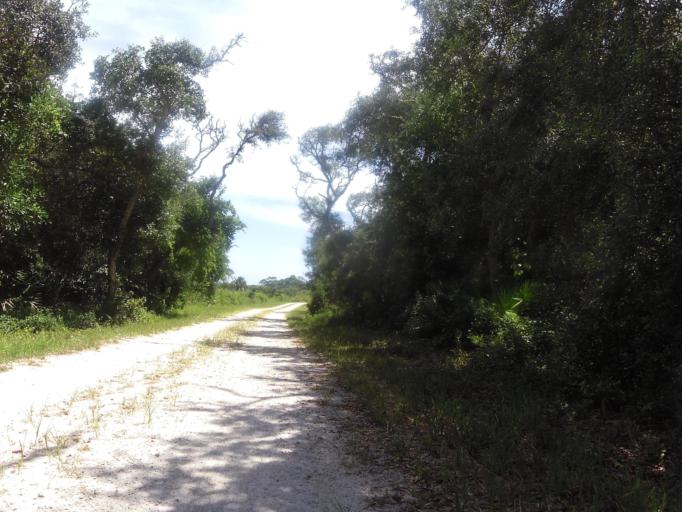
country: US
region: Florida
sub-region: Saint Johns County
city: Villano Beach
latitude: 30.0392
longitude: -81.3370
